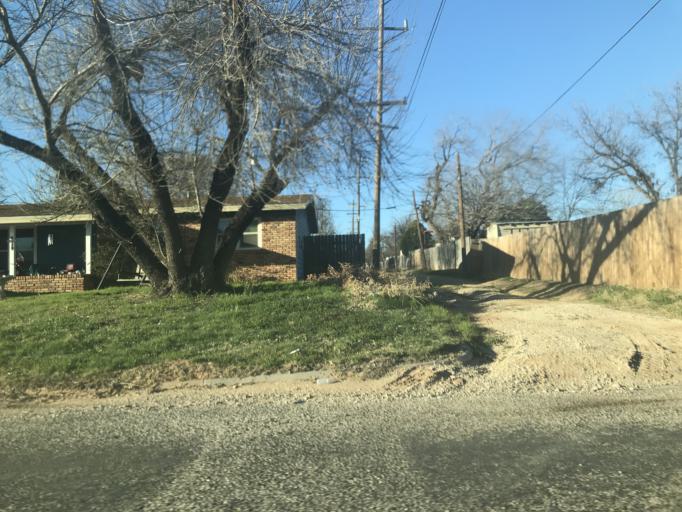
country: US
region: Texas
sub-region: Tom Green County
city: San Angelo
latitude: 31.4384
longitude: -100.4762
